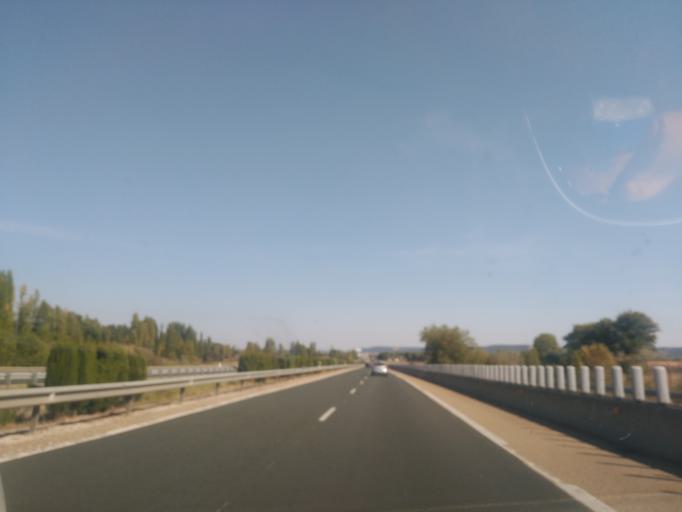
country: ES
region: Castille and Leon
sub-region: Provincia de Valladolid
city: Tudela de Duero
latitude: 41.5933
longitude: -4.6165
